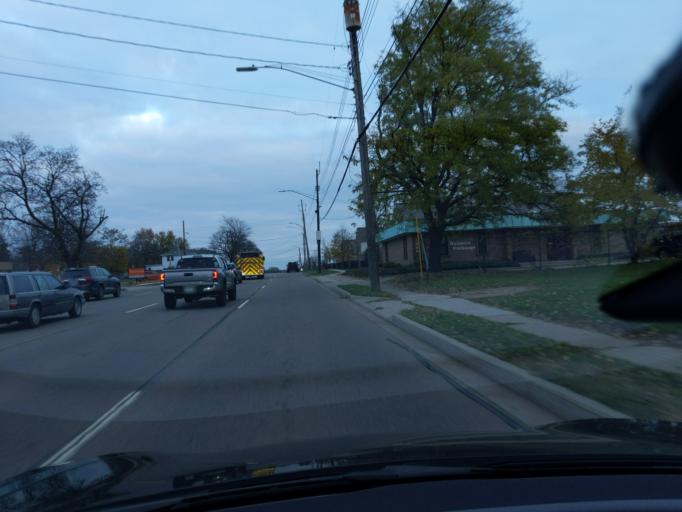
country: US
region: Michigan
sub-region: Ingham County
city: Lansing
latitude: 42.7408
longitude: -84.5348
